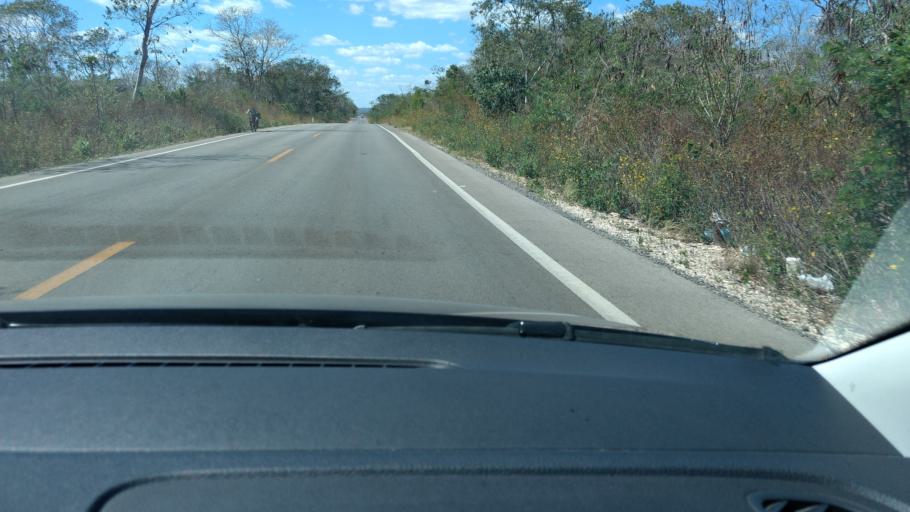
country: MX
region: Yucatan
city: Tzucacab
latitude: 20.0825
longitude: -89.0741
